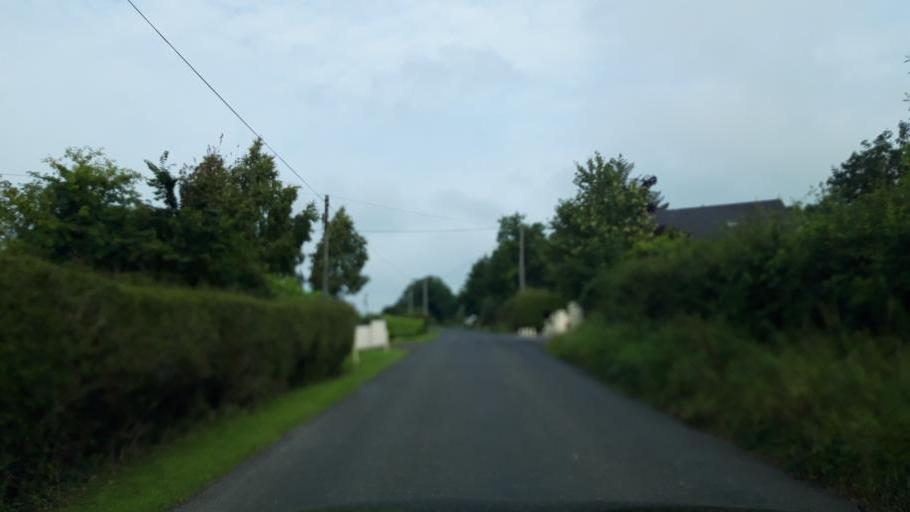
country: IE
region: Munster
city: Fethard
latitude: 52.5850
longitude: -7.5915
